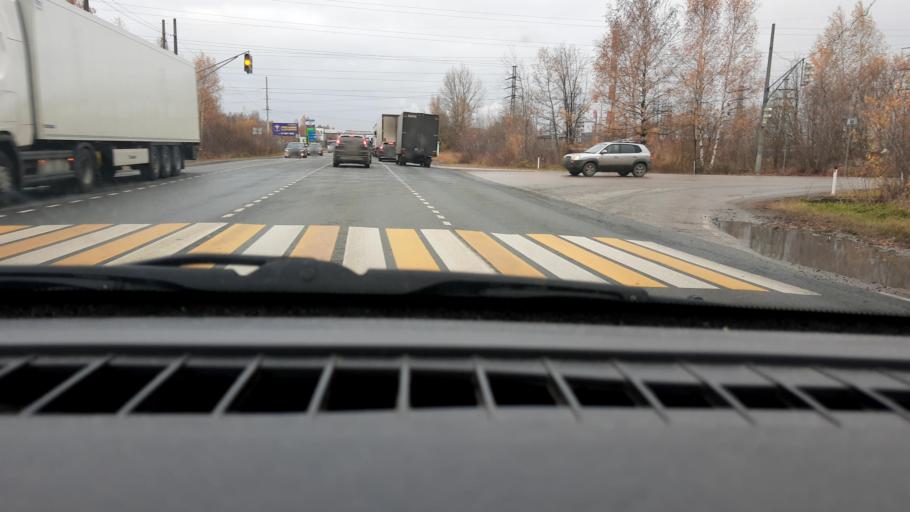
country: RU
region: Nizjnij Novgorod
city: Kstovo
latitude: 56.1171
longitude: 44.1525
